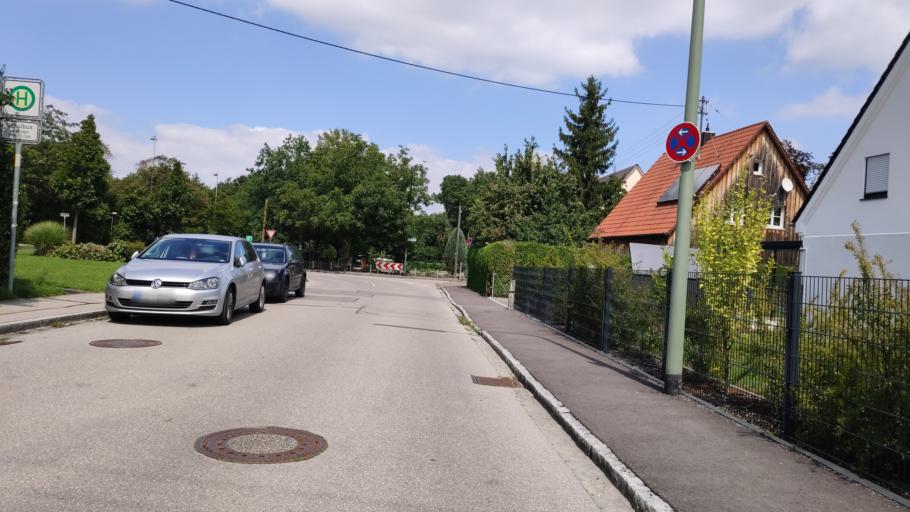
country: DE
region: Bavaria
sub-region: Swabia
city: Konigsbrunn
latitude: 48.2695
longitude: 10.8991
